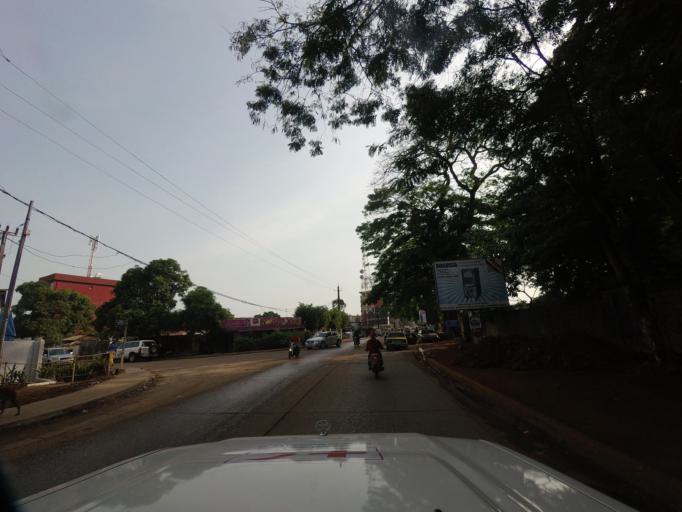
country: GN
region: Conakry
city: Camayenne
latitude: 9.5332
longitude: -13.6866
